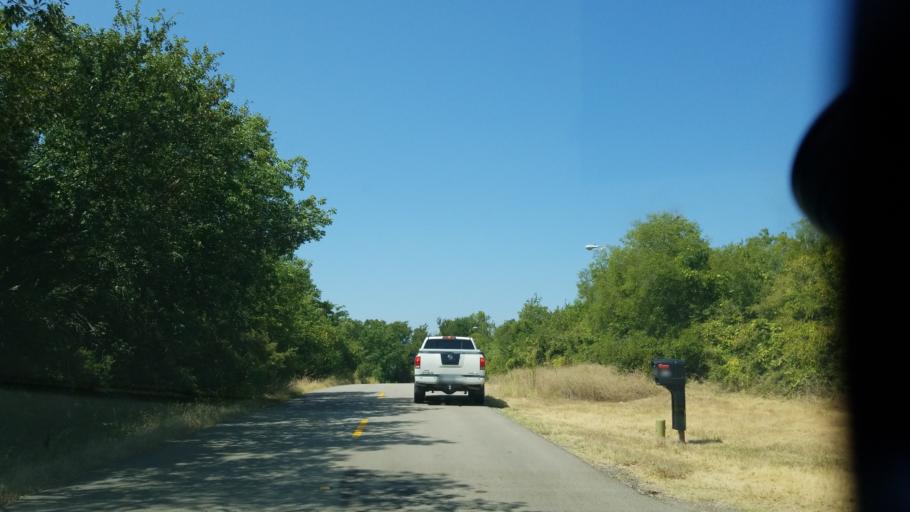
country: US
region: Texas
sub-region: Dallas County
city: Cockrell Hill
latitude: 32.7114
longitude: -96.9184
